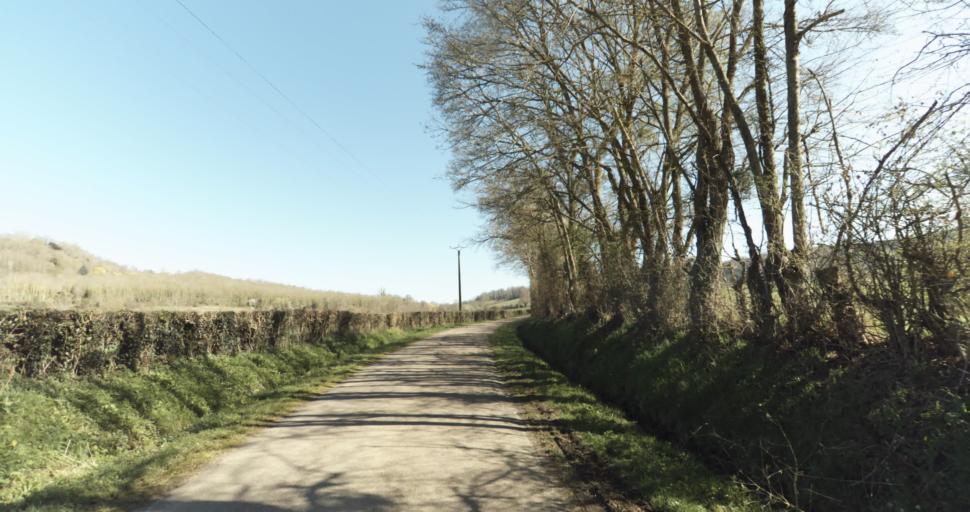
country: FR
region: Lower Normandy
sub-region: Departement du Calvados
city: Saint-Pierre-sur-Dives
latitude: 48.9749
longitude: 0.0531
